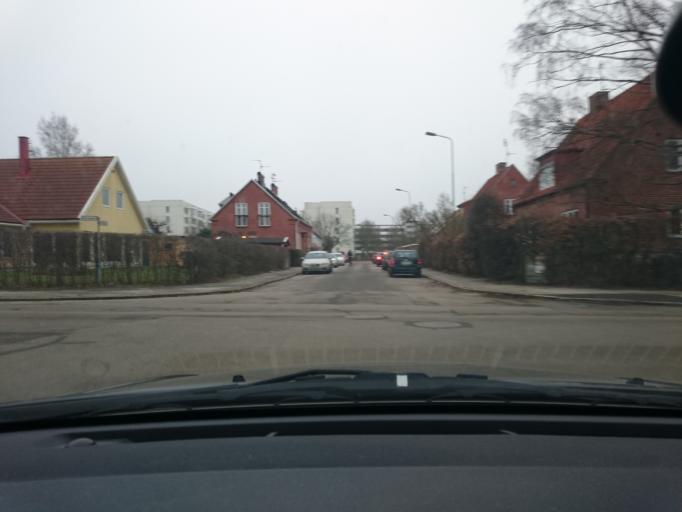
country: SE
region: Skane
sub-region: Lunds Kommun
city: Lund
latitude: 55.7064
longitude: 13.1741
